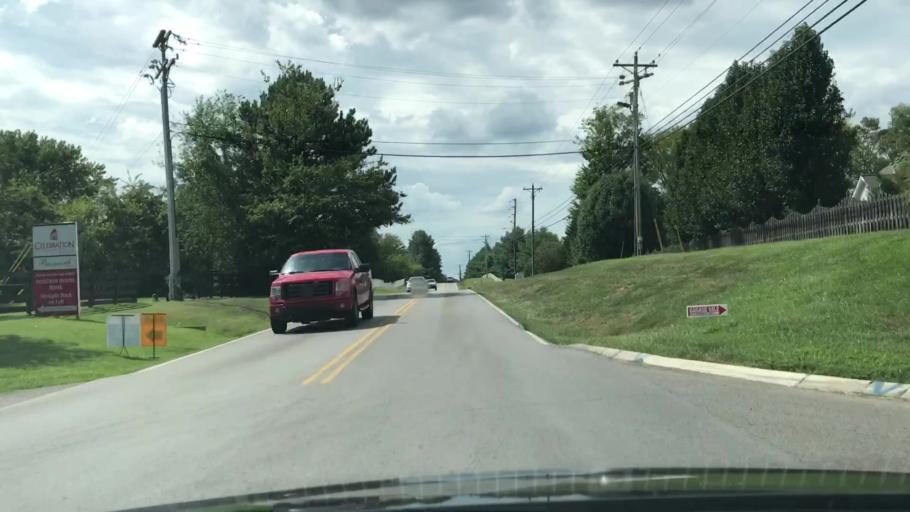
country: US
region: Tennessee
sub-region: Williamson County
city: Thompson's Station
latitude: 35.7816
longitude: -86.8928
